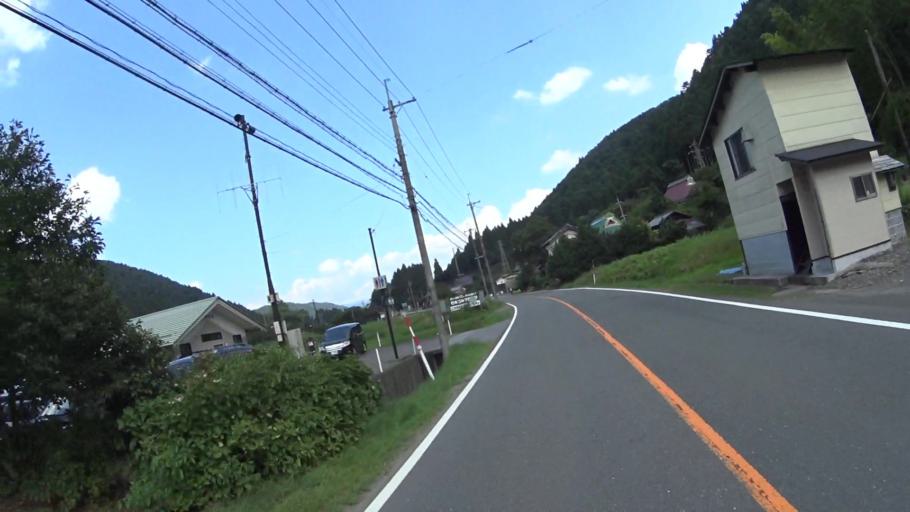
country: JP
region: Shiga Prefecture
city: Kitahama
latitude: 35.3239
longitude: 135.8981
